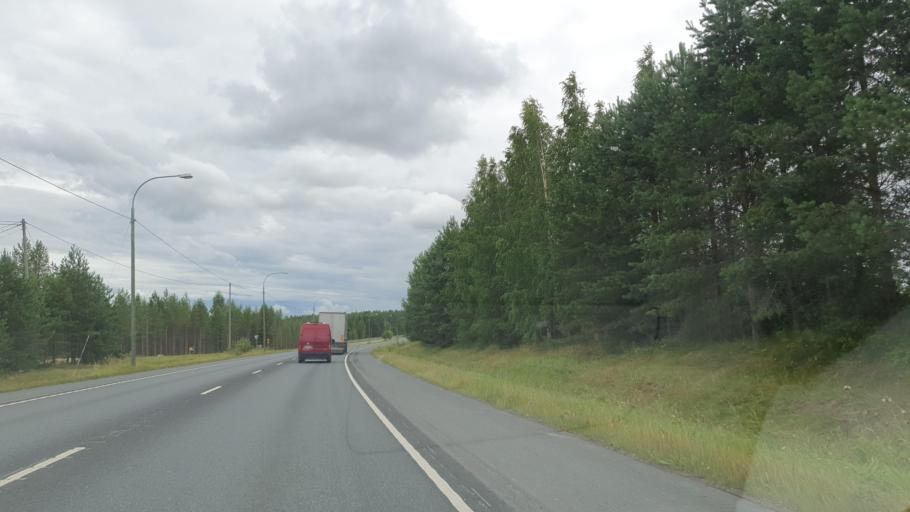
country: FI
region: Northern Savo
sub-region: Ylae-Savo
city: Iisalmi
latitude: 63.4874
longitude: 27.2874
